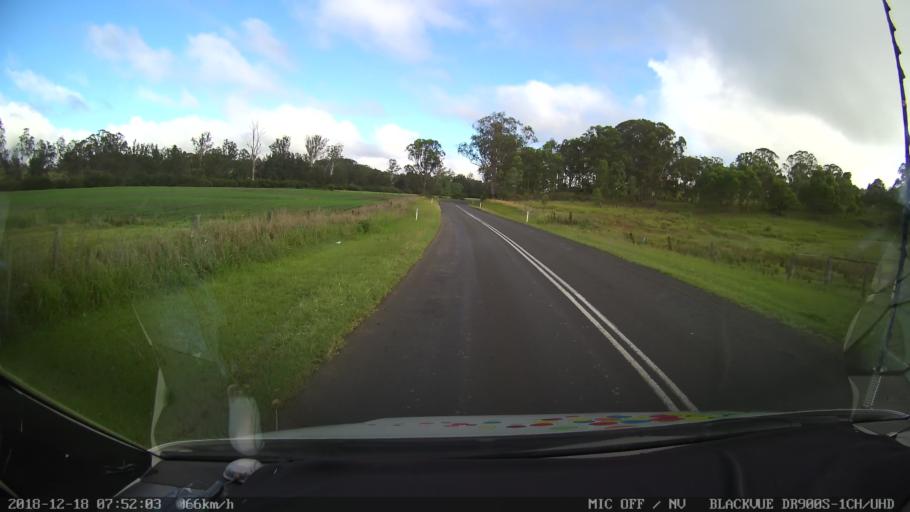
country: AU
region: New South Wales
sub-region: Kyogle
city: Kyogle
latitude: -28.4323
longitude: 152.5809
